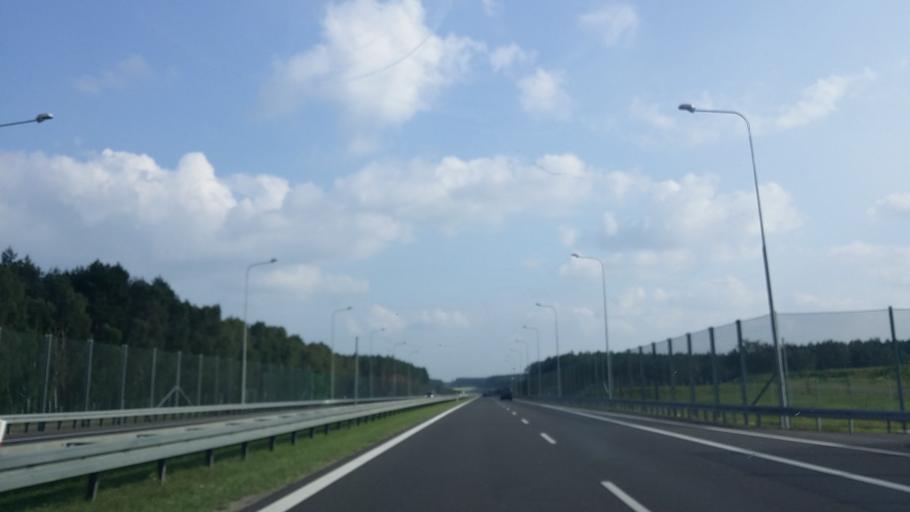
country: PL
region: Lubusz
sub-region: Powiat miedzyrzecki
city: Skwierzyna
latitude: 52.5381
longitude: 15.5419
